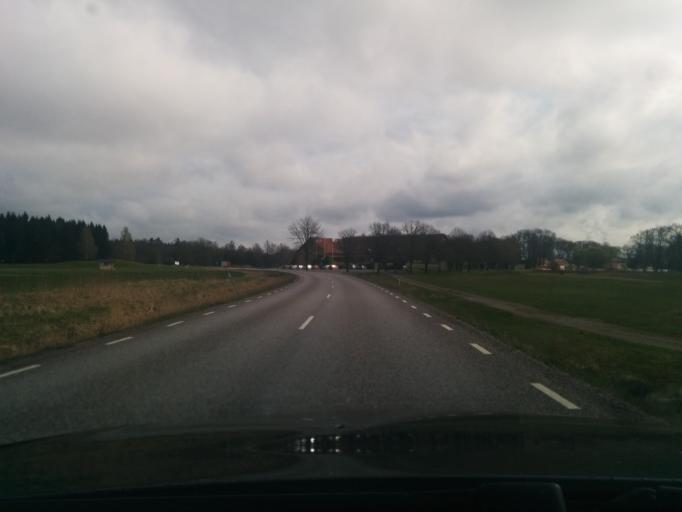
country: SE
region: Uppsala
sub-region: Tierps Kommun
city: Orbyhus
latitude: 60.1985
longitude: 17.6978
